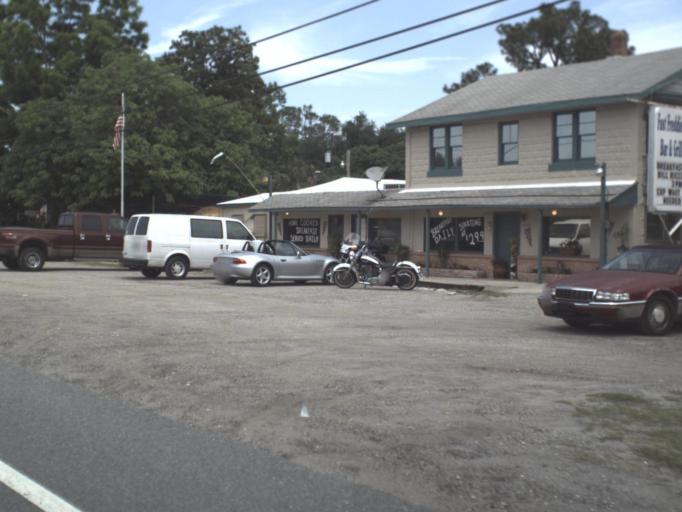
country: US
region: Florida
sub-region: Duval County
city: Jacksonville
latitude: 30.4706
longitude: -81.6316
